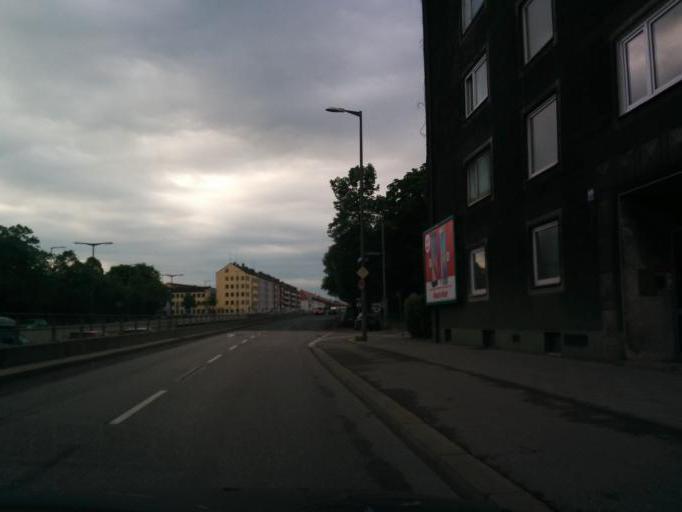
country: DE
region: Bavaria
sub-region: Upper Bavaria
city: Munich
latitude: 48.1060
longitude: 11.5809
